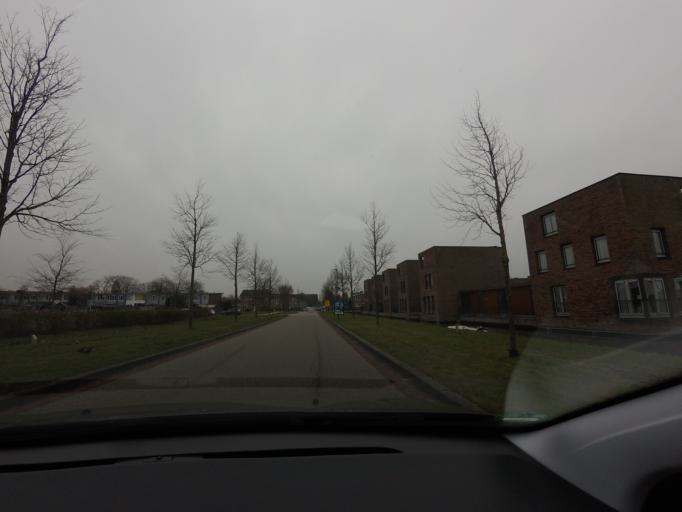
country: NL
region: Friesland
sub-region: Sudwest Fryslan
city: Bolsward
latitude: 53.0666
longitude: 5.5168
